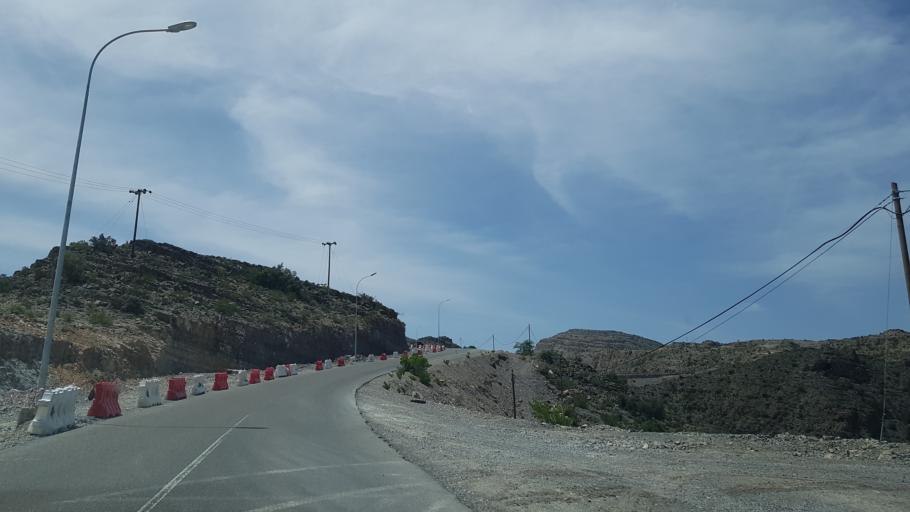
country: OM
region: Muhafazat ad Dakhiliyah
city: Izki
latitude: 23.0949
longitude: 57.6796
